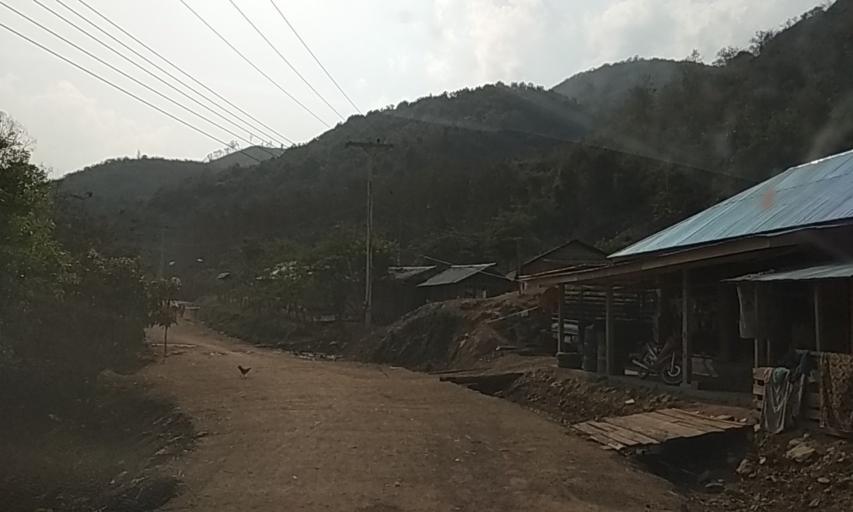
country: LA
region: Louangphabang
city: Louangphabang
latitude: 20.0526
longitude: 101.8532
